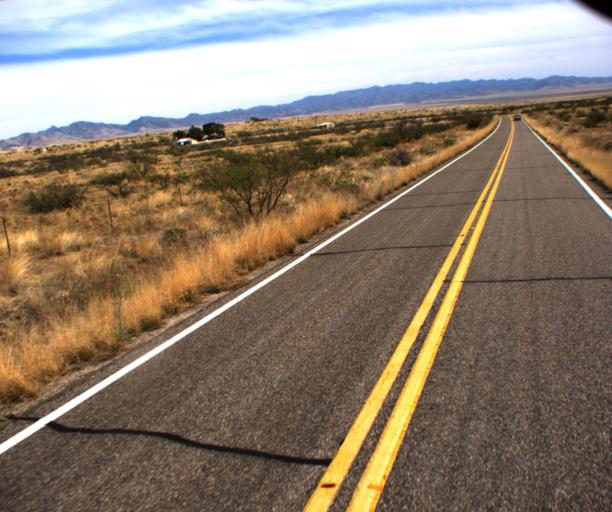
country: US
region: Arizona
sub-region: Cochise County
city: Willcox
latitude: 32.1349
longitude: -109.5609
